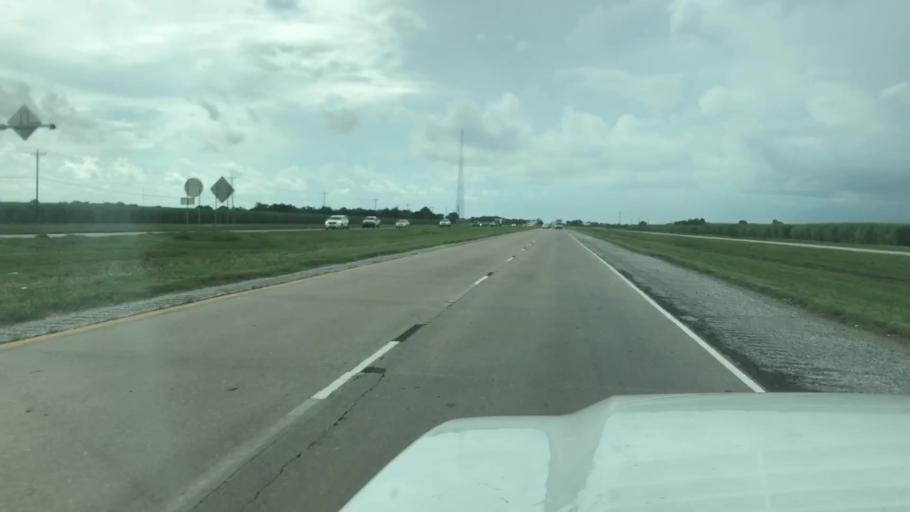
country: US
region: Louisiana
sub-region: Iberia Parish
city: Jeanerette
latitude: 29.9134
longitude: -91.7188
